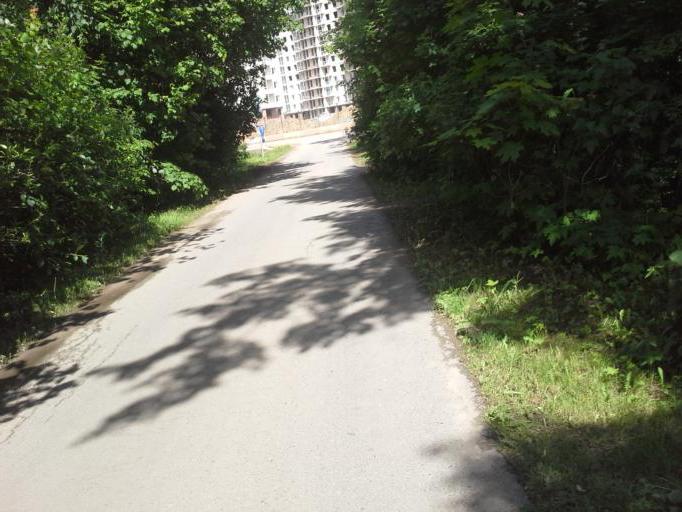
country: RU
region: Moskovskaya
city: Annino
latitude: 55.6172
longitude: 37.2596
